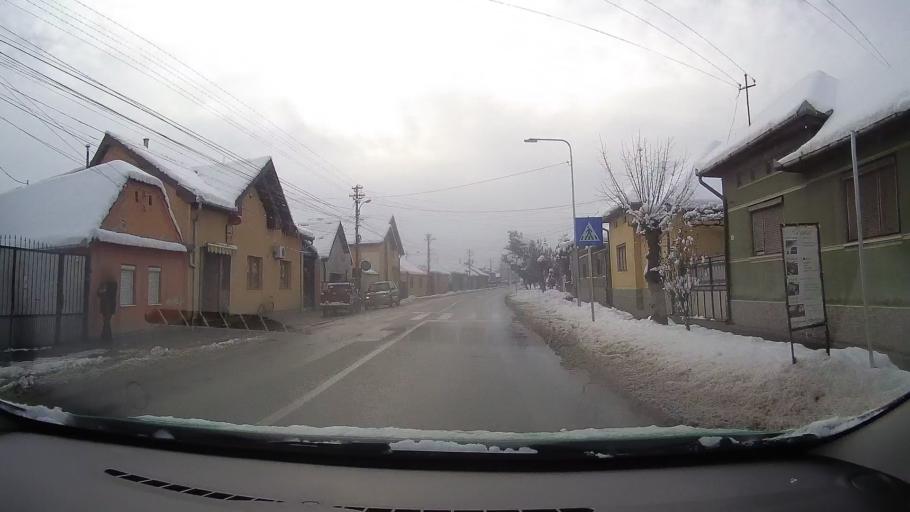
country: RO
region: Alba
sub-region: Municipiul Sebes
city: Sebes
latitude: 45.9495
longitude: 23.5655
